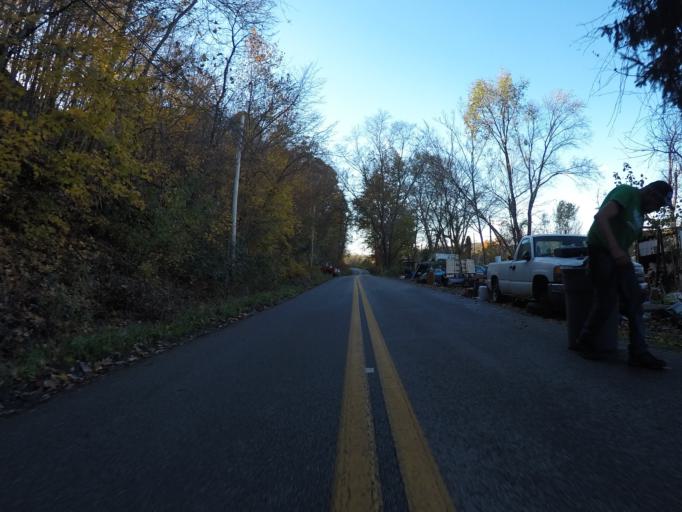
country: US
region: Ohio
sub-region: Lawrence County
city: Burlington
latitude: 38.3958
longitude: -82.5238
